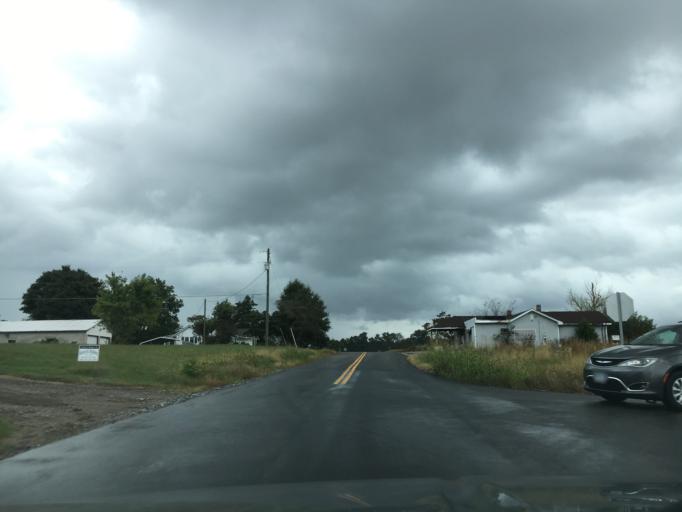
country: US
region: Virginia
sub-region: Amelia County
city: Amelia Court House
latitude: 37.4217
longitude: -77.9592
